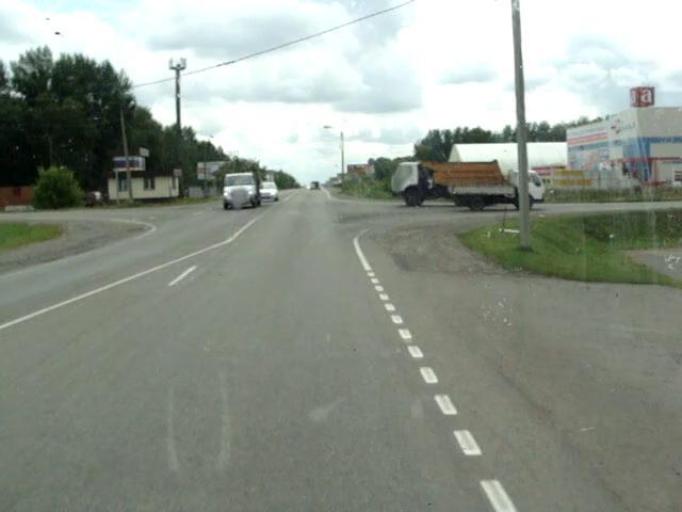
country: RU
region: Altai Krai
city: Zarya
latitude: 52.5753
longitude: 85.1803
